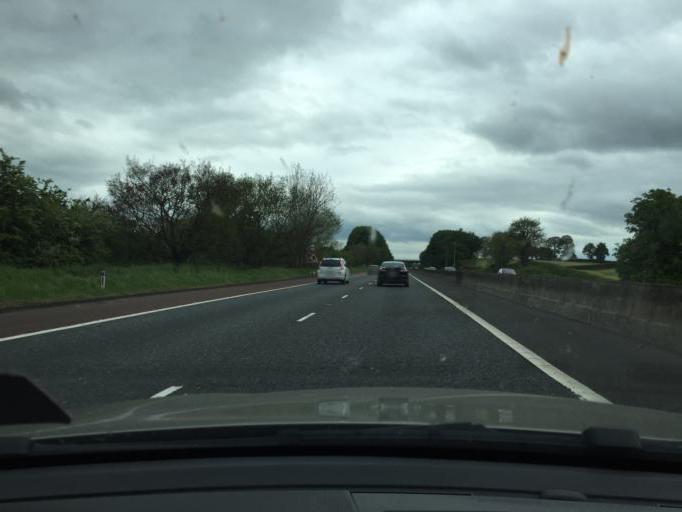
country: GB
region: Northern Ireland
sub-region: Lisburn District
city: Lisburn
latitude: 54.5374
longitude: -5.9958
